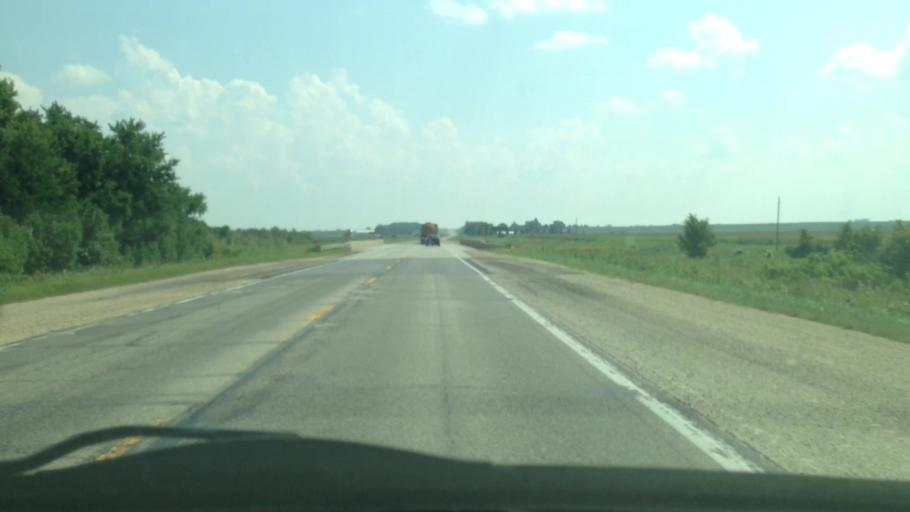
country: US
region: Iowa
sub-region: Chickasaw County
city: New Hampton
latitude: 43.2404
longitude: -92.2989
